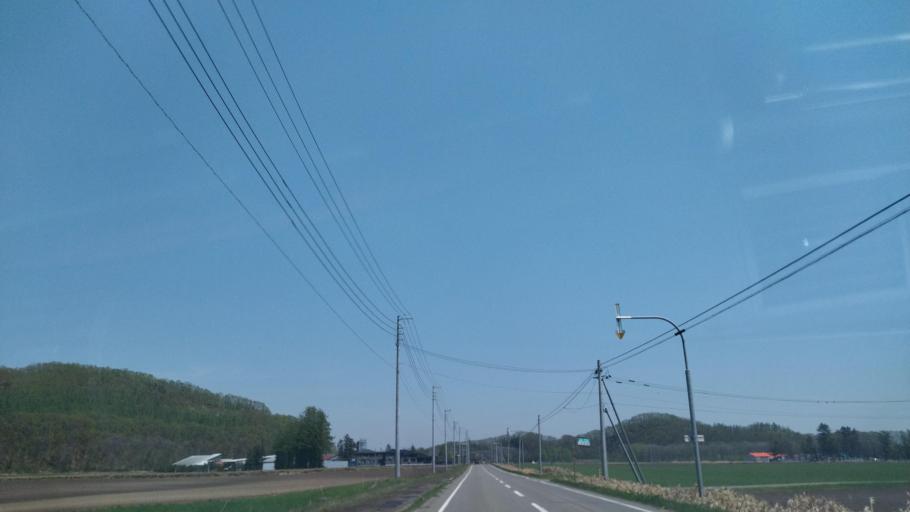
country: JP
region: Hokkaido
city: Obihiro
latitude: 42.8181
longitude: 142.9793
